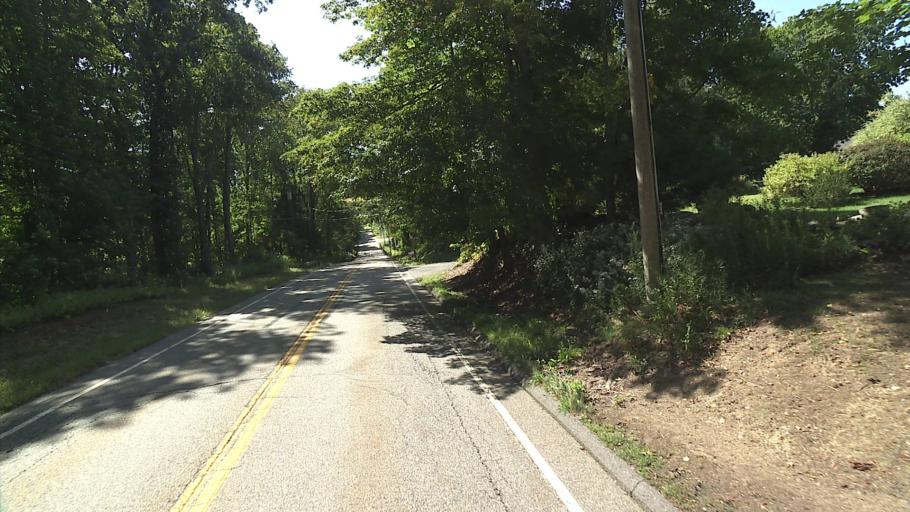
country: US
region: Connecticut
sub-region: Litchfield County
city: Northwest Harwinton
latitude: 41.7373
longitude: -73.0765
